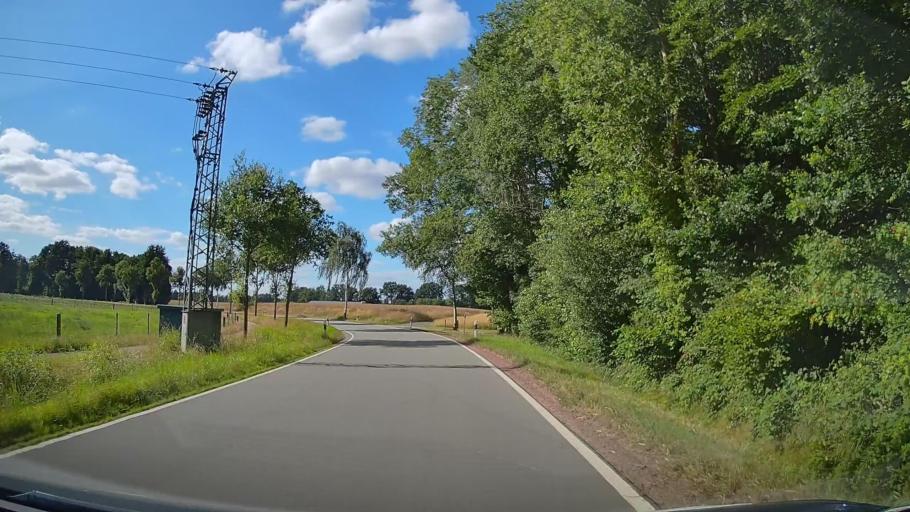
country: DE
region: Lower Saxony
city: Menslage
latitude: 52.6847
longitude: 7.7840
